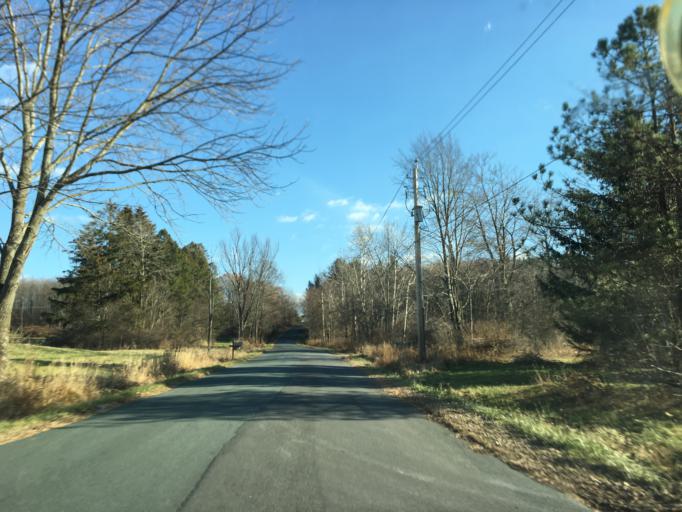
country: US
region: New York
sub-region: Rensselaer County
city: West Sand Lake
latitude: 42.6010
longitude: -73.5971
